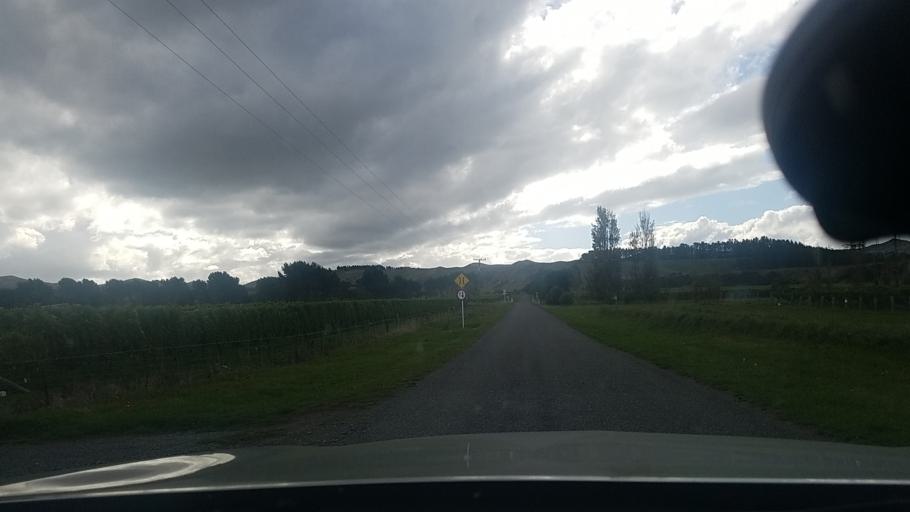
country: NZ
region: Marlborough
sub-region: Marlborough District
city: Blenheim
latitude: -41.6098
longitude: 174.1331
